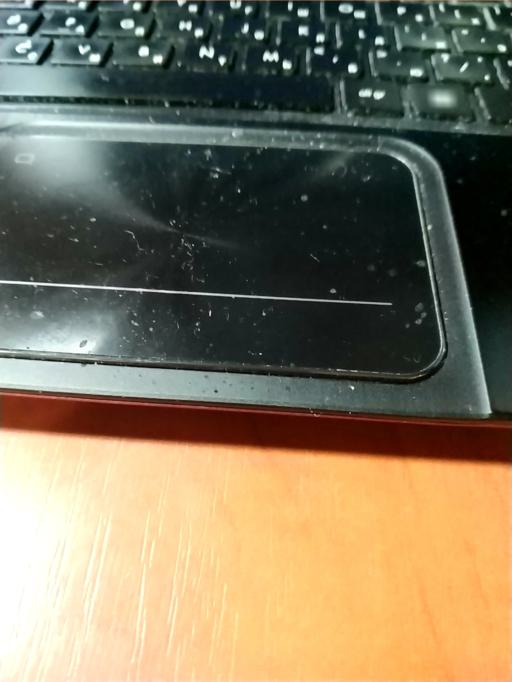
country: RU
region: Arkhangelskaya
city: Kargopol'
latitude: 60.9347
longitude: 38.8811
